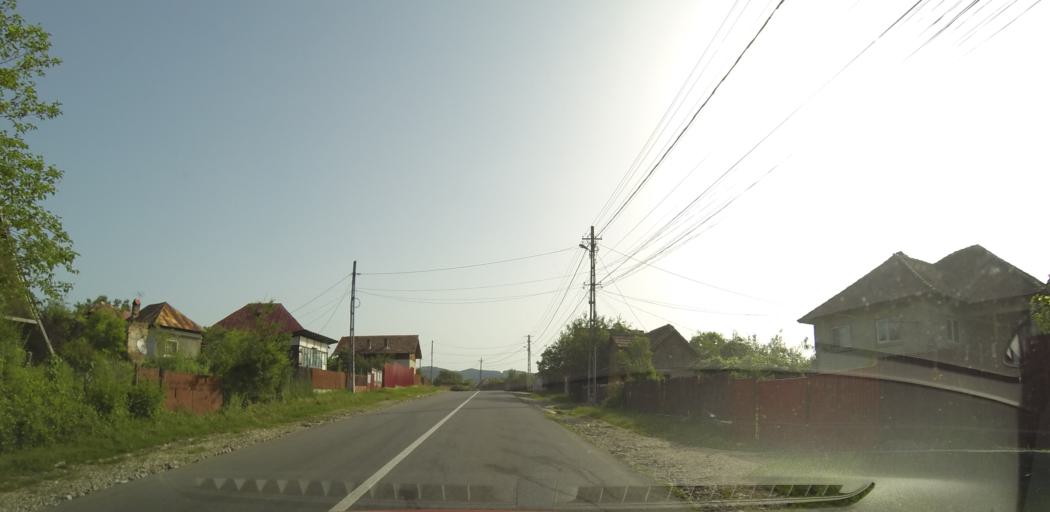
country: RO
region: Valcea
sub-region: Comuna Pausesti-Maglasi
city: Pausesti-Maglasi
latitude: 45.1588
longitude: 24.2495
